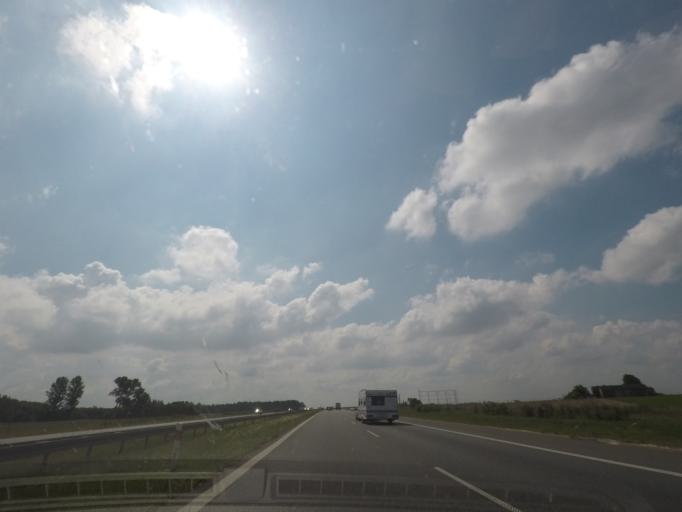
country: PL
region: Lodz Voivodeship
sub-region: Powiat kutnowski
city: Krzyzanow
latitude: 52.1994
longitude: 19.4858
